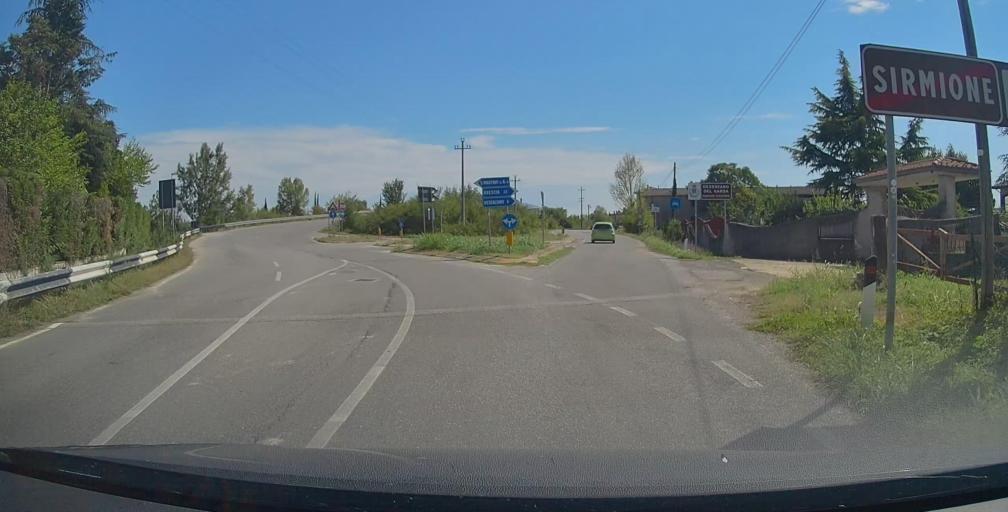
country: IT
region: Lombardy
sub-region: Provincia di Brescia
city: San Martino della Battaglia
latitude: 45.4460
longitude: 10.6171
